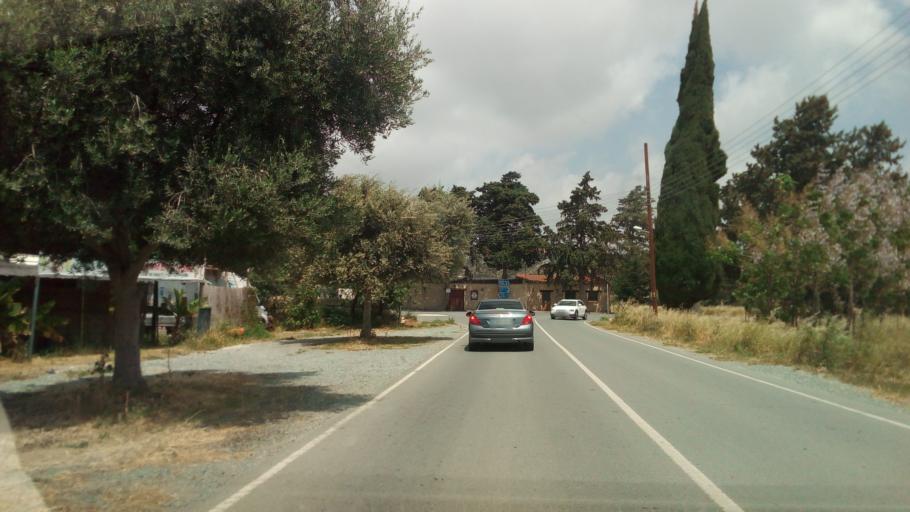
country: CY
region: Limassol
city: Pissouri
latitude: 34.6748
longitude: 32.7212
